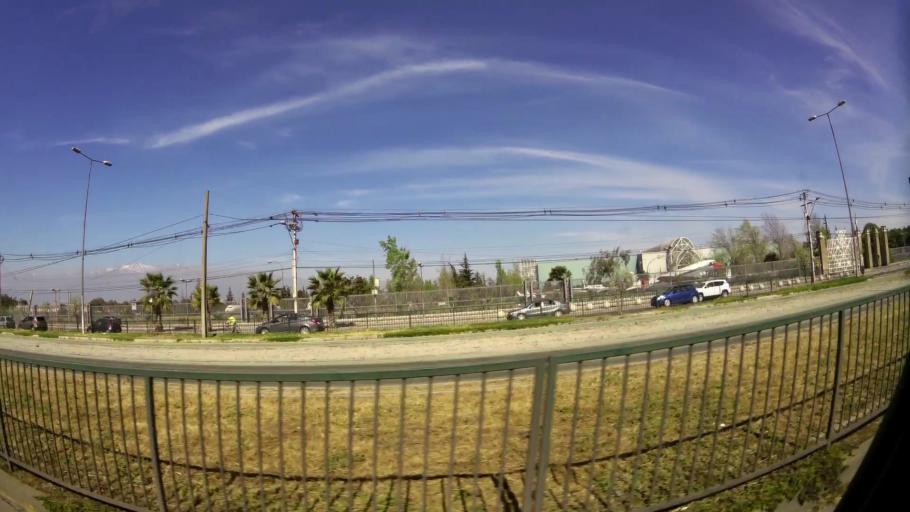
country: CL
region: Santiago Metropolitan
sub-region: Provincia de Santiago
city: Lo Prado
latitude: -33.4856
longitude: -70.6978
